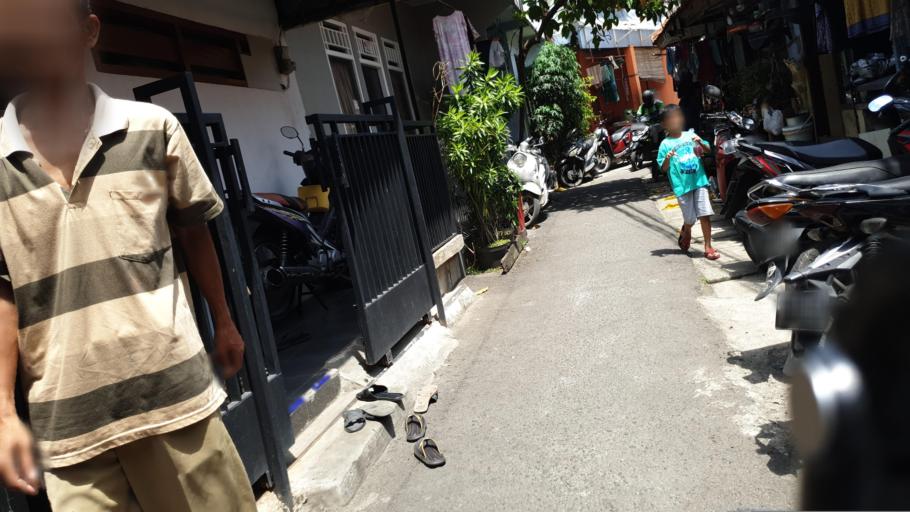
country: ID
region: Jakarta Raya
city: Jakarta
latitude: -6.2499
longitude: 106.7885
